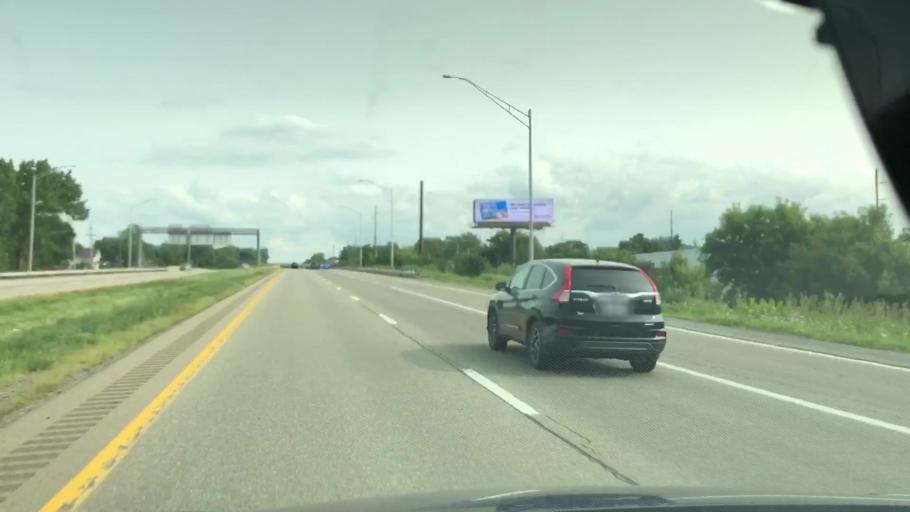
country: US
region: Pennsylvania
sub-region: Erie County
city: Erie
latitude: 42.0910
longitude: -80.1198
